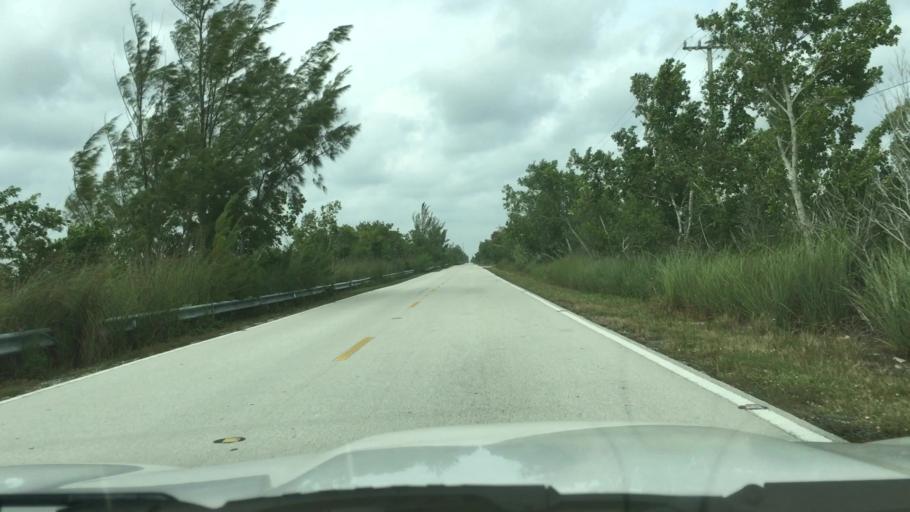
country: US
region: Florida
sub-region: Miami-Dade County
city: Florida City
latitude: 25.3513
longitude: -80.4196
